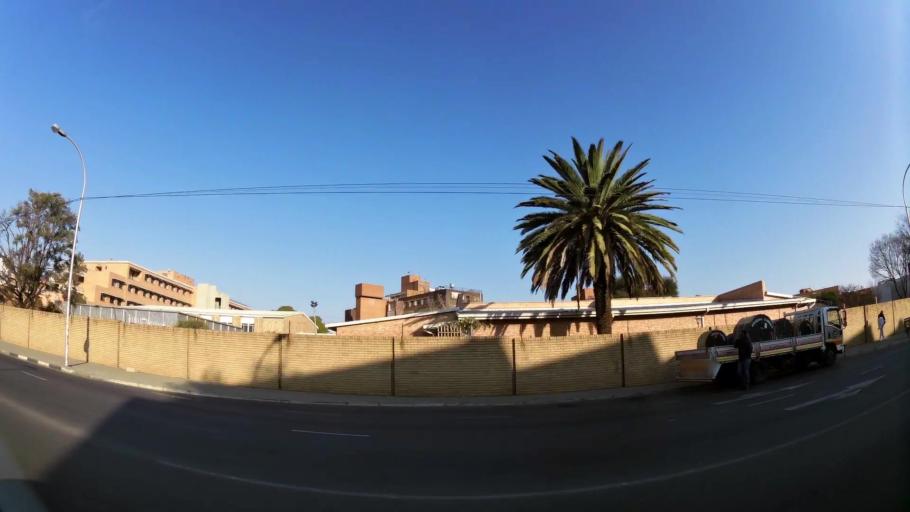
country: ZA
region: Gauteng
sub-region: Ekurhuleni Metropolitan Municipality
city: Germiston
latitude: -26.2194
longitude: 28.1656
